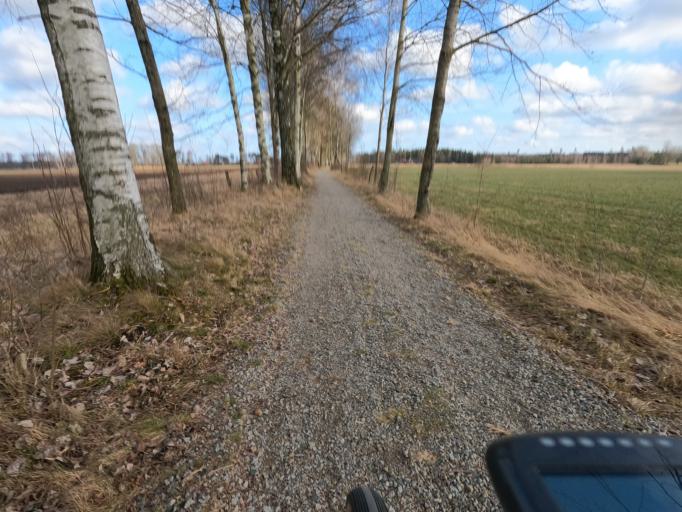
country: SE
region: Kronoberg
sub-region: Alvesta Kommun
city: Vislanda
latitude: 56.7282
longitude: 14.5648
